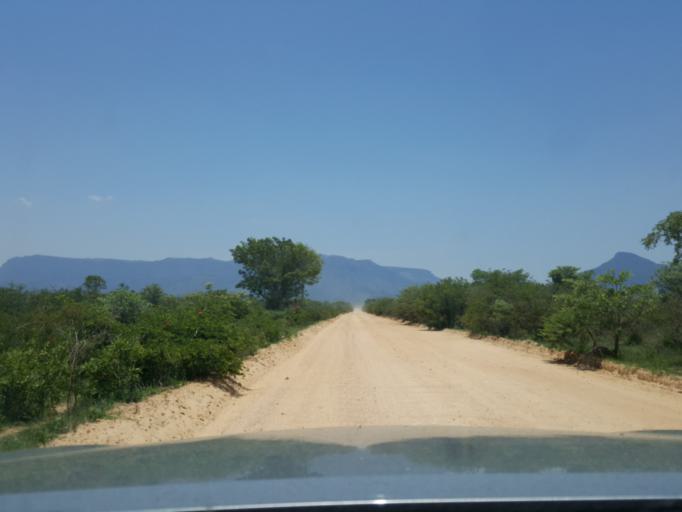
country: ZA
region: Limpopo
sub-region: Mopani District Municipality
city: Hoedspruit
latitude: -24.5663
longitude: 31.0093
